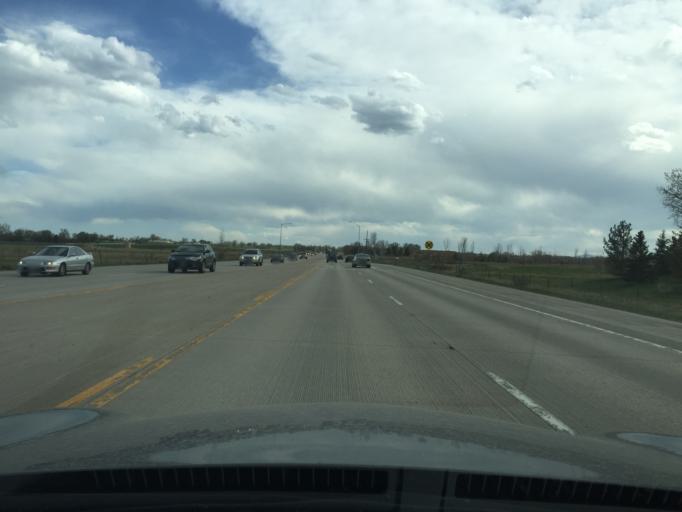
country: US
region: Colorado
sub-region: Boulder County
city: Erie
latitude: 40.0519
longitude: -105.1028
